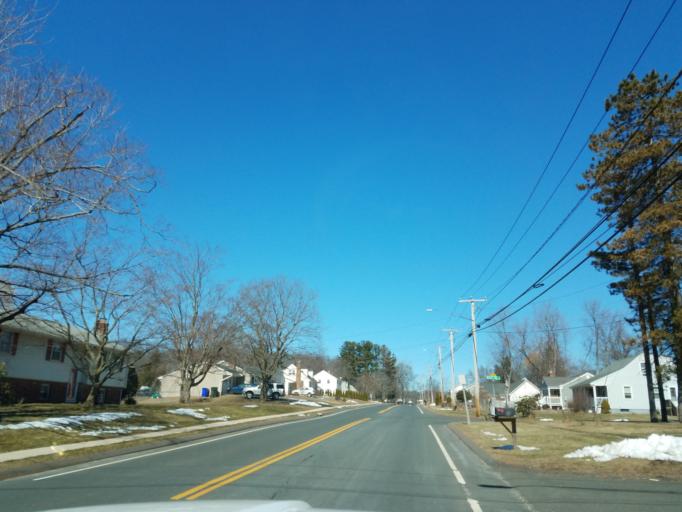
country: US
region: Connecticut
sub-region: Hartford County
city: Windsor Locks
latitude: 41.9077
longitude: -72.6361
